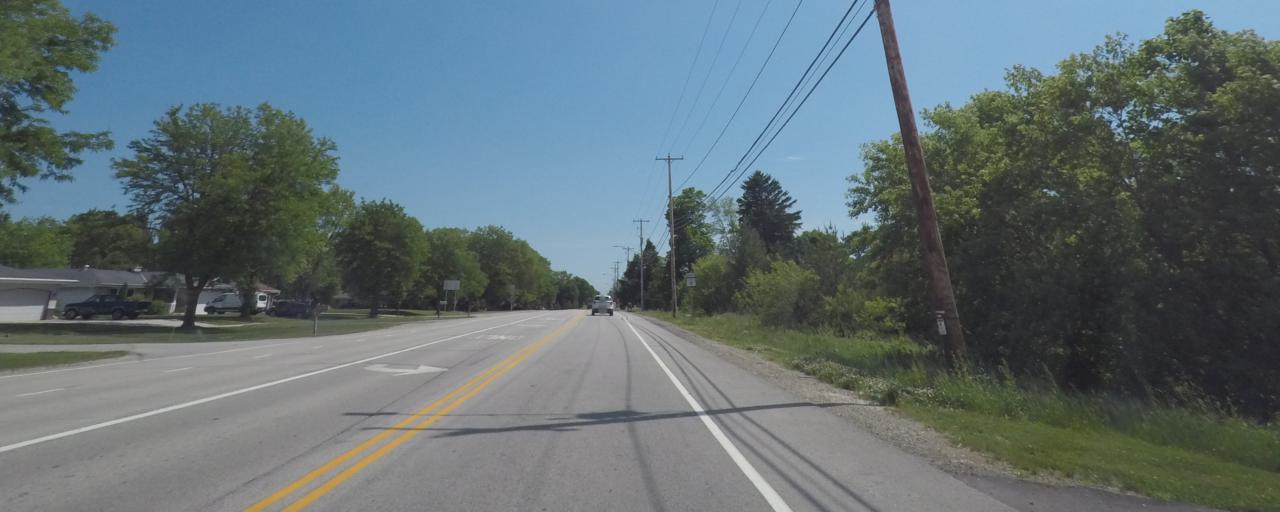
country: US
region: Wisconsin
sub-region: Milwaukee County
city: Oak Creek
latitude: 42.9011
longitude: -87.9312
